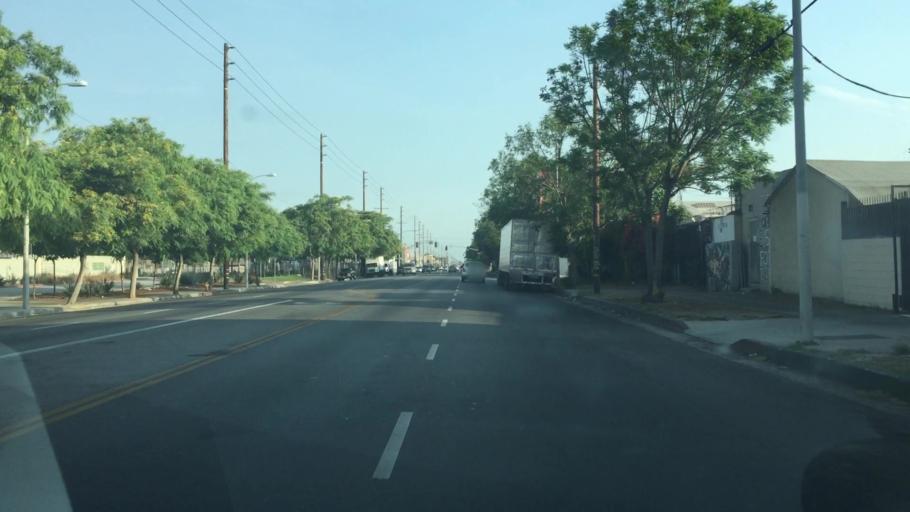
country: US
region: California
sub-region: Los Angeles County
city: Florence-Graham
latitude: 33.9841
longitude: -118.2565
